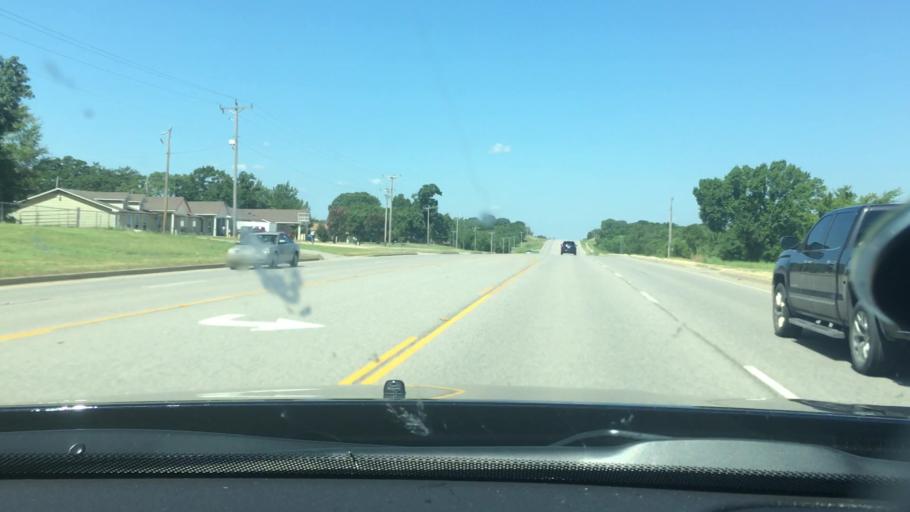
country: US
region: Oklahoma
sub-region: Bryan County
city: Calera
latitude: 33.9982
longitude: -96.5335
